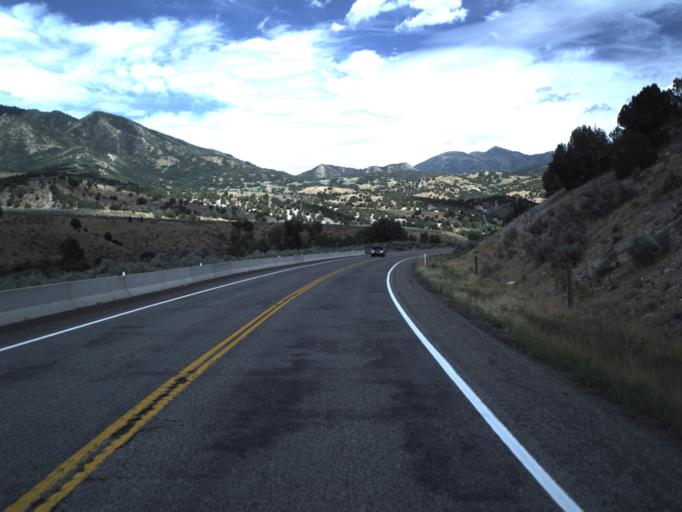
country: US
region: Utah
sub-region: Utah County
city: Woodland Hills
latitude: 39.9338
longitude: -111.5439
